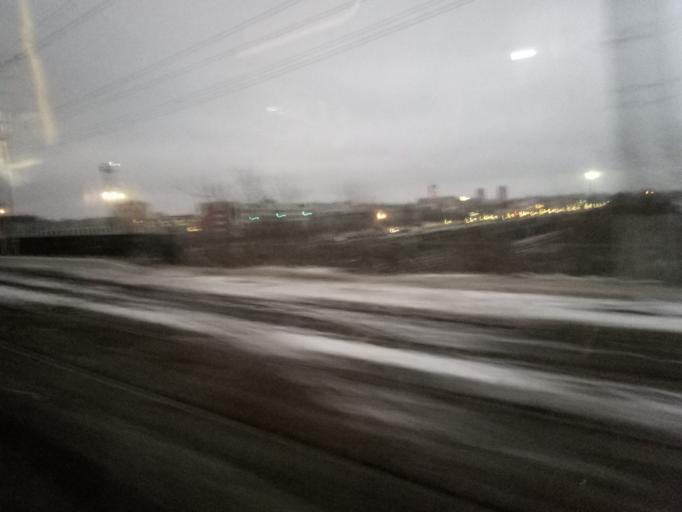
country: RU
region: Tula
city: Tula
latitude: 54.2054
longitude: 37.5817
